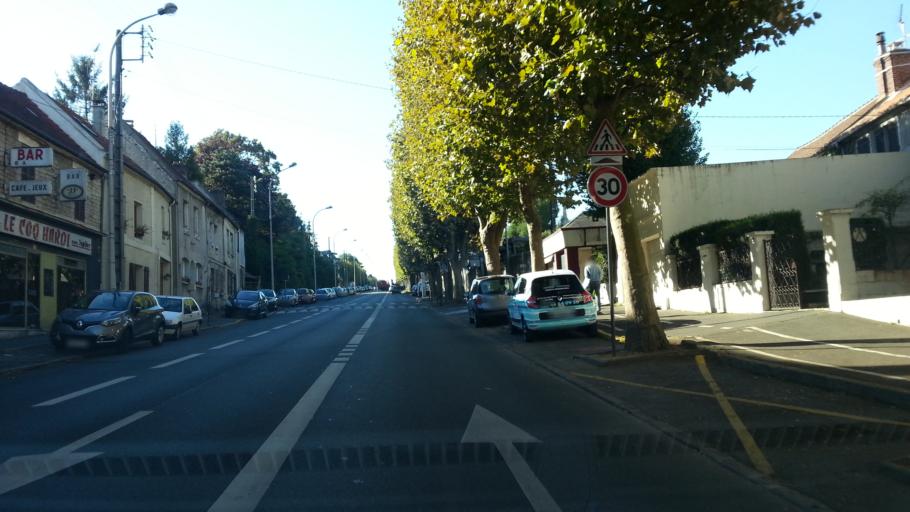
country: FR
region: Picardie
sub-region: Departement de l'Oise
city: Creil
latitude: 49.2562
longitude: 2.4786
